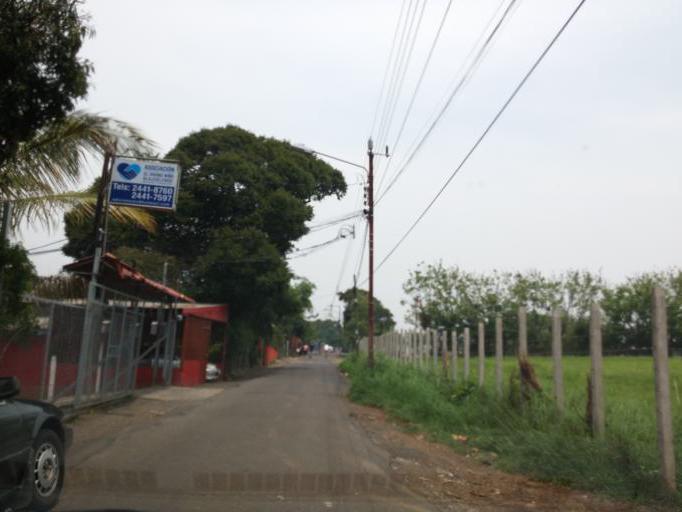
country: CR
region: Heredia
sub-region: Canton de Belen
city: San Antonio
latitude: 9.9929
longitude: -84.2019
